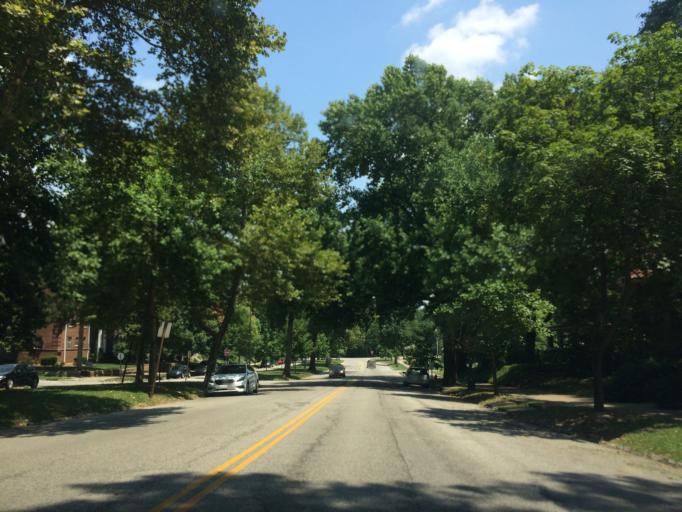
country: US
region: Kentucky
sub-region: Jefferson County
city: Audubon Park
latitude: 38.2356
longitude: -85.7117
